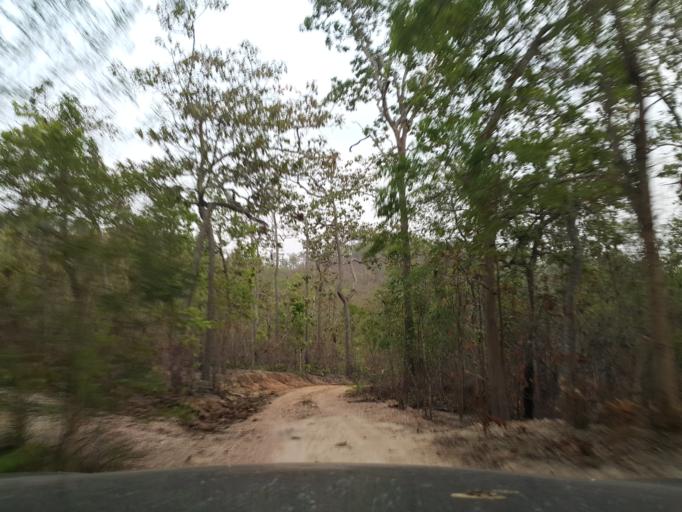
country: TH
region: Lamphun
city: Thung Hua Chang
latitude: 17.9077
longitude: 99.0815
